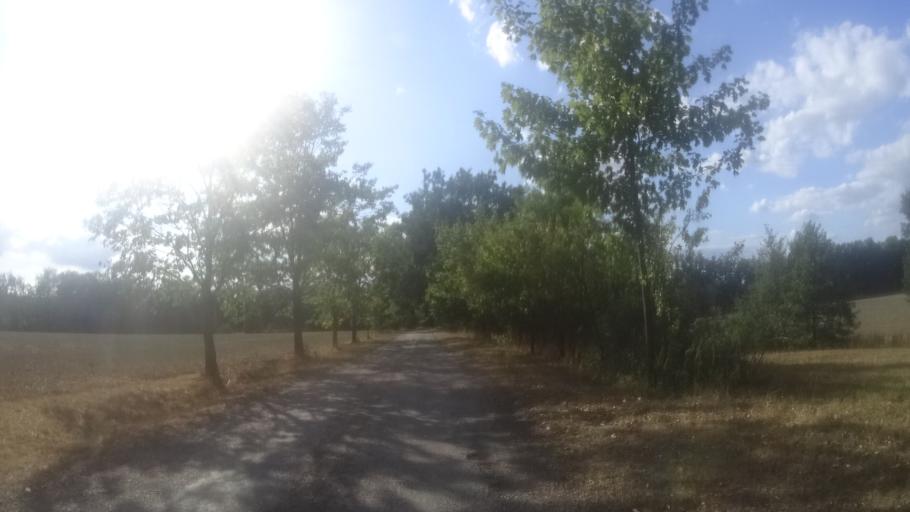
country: CZ
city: Albrechtice nad Orlici
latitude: 50.1567
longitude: 16.0433
